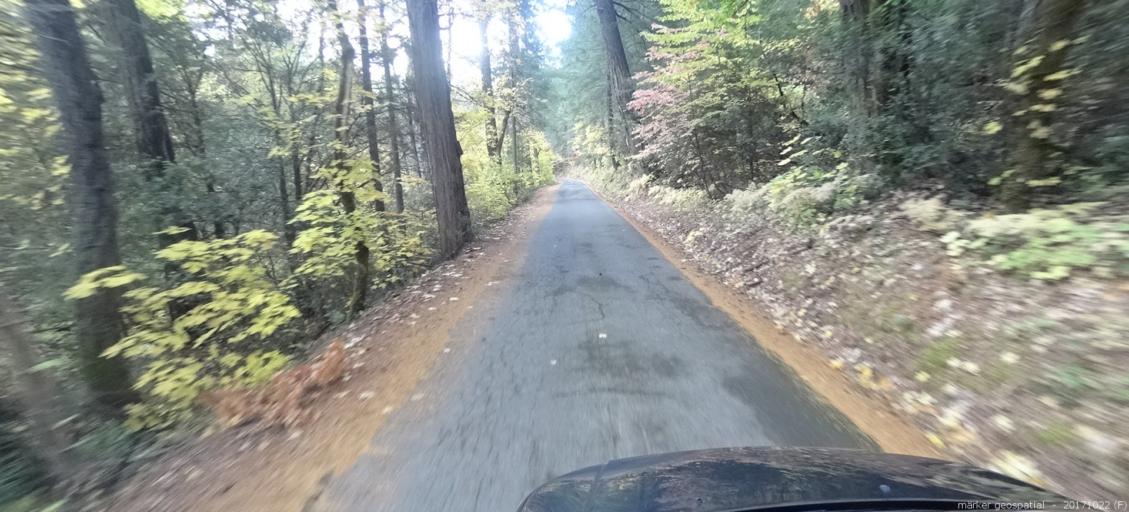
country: US
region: California
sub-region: Siskiyou County
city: Dunsmuir
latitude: 41.1698
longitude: -122.2795
